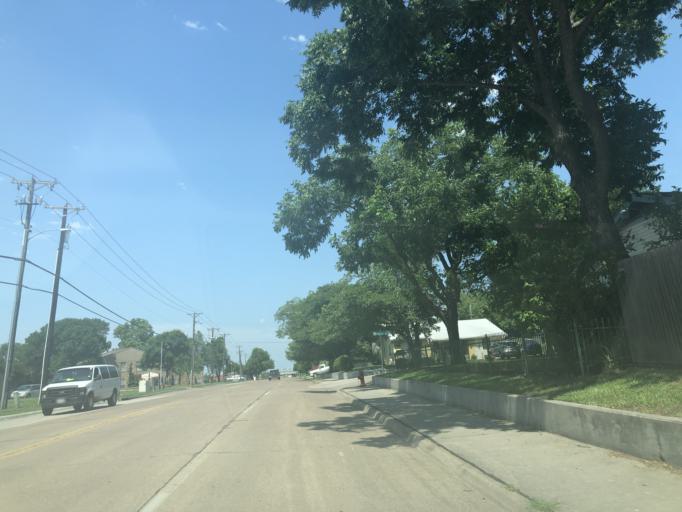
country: US
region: Texas
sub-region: Dallas County
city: Grand Prairie
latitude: 32.7288
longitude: -97.0107
